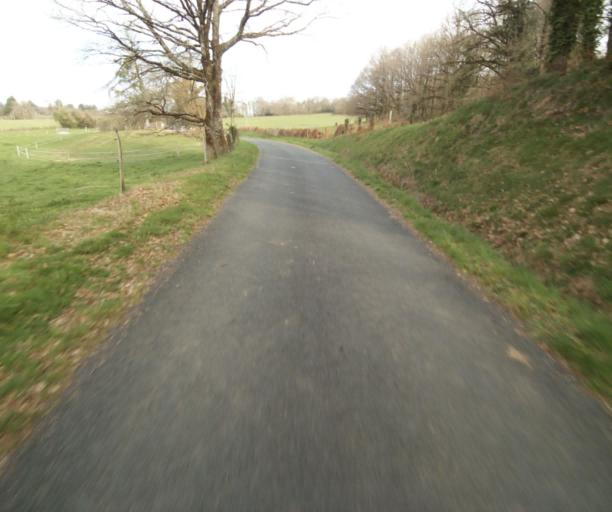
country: FR
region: Limousin
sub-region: Departement de la Correze
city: Chamboulive
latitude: 45.4483
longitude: 1.7544
